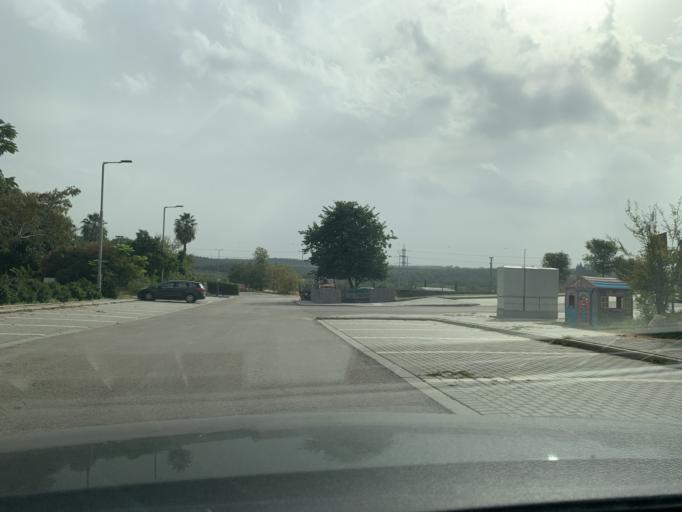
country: IL
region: Central District
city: Tirah
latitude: 32.2161
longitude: 34.9350
